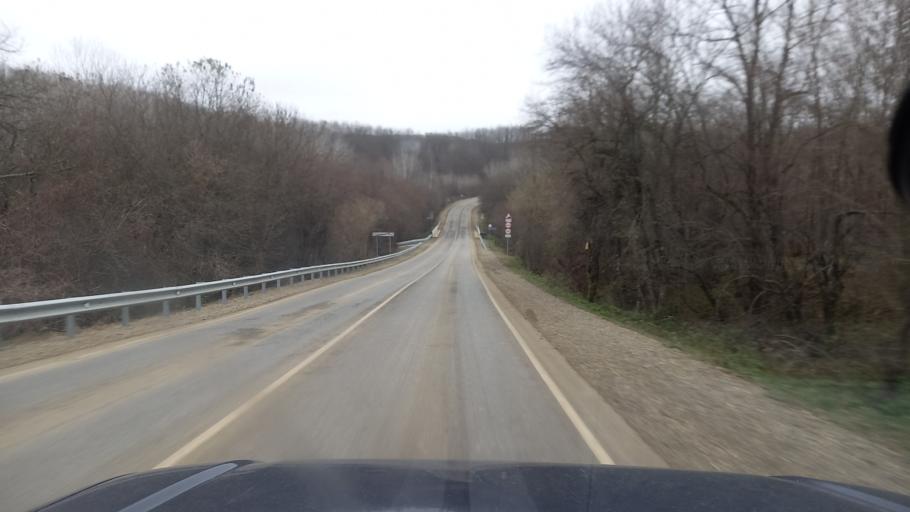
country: RU
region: Krasnodarskiy
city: Saratovskaya
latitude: 44.5435
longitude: 39.2943
